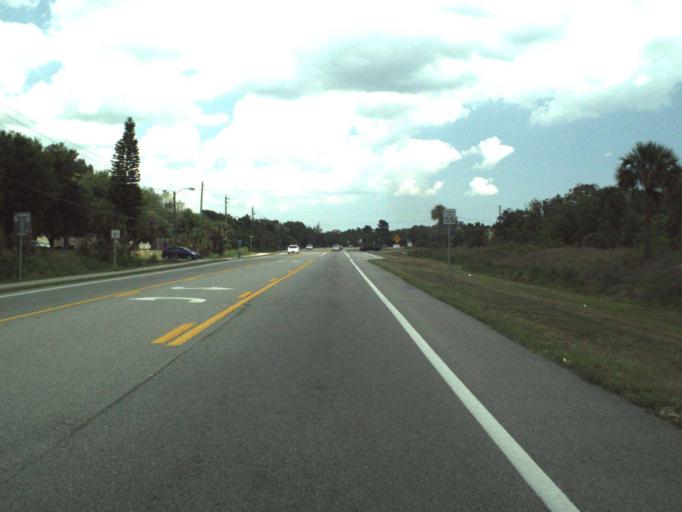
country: US
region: Florida
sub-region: Brevard County
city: Titusville
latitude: 28.5878
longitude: -80.8469
